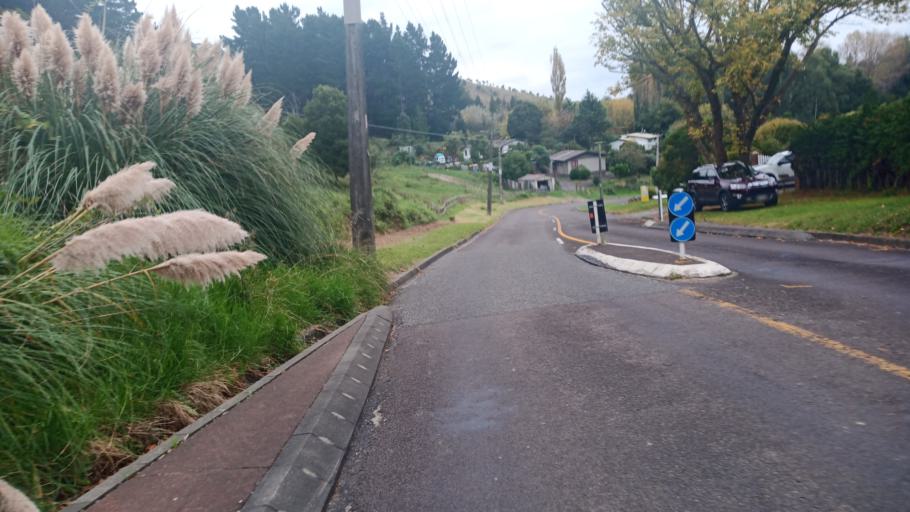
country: NZ
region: Gisborne
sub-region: Gisborne District
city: Gisborne
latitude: -38.6822
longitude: 178.0400
